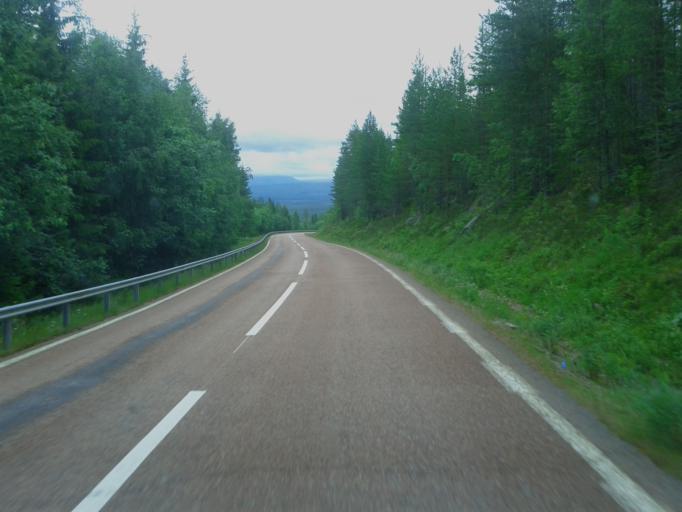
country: NO
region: Hedmark
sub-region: Trysil
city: Innbygda
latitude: 61.8485
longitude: 12.6067
